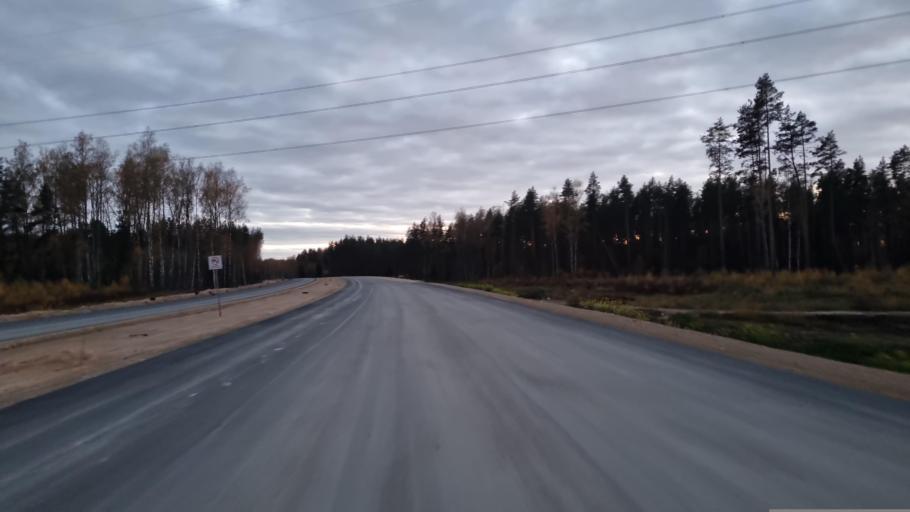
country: LV
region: Kekava
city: Balozi
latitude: 56.8642
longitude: 24.1609
